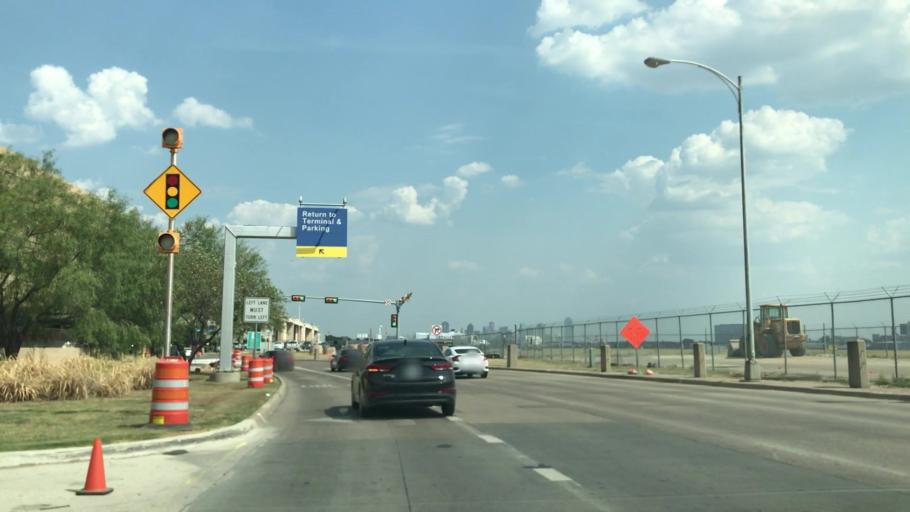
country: US
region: Texas
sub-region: Dallas County
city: University Park
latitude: 32.8403
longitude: -96.8476
